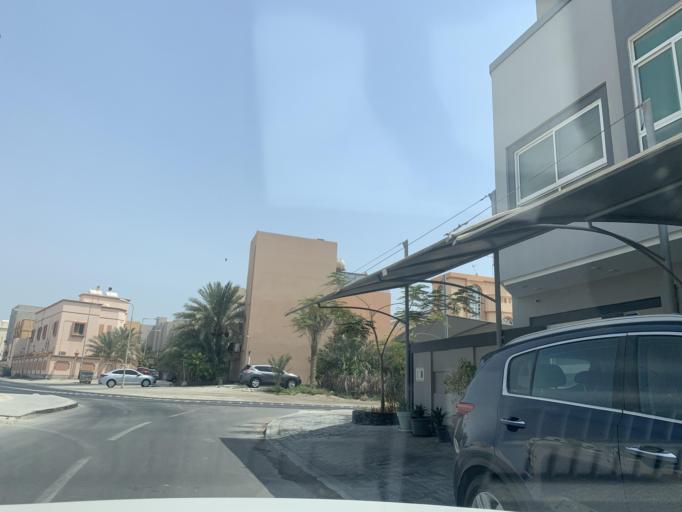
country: BH
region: Manama
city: Jidd Hafs
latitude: 26.2096
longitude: 50.5028
